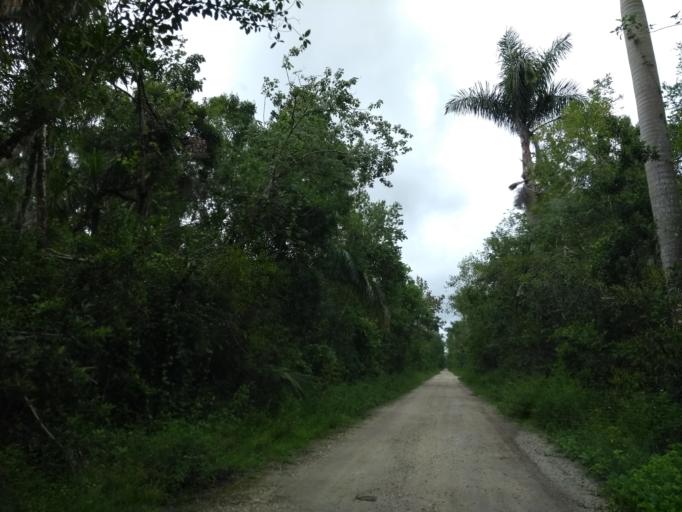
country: US
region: Florida
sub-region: Collier County
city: Lely Resort
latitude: 26.0014
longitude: -81.4112
